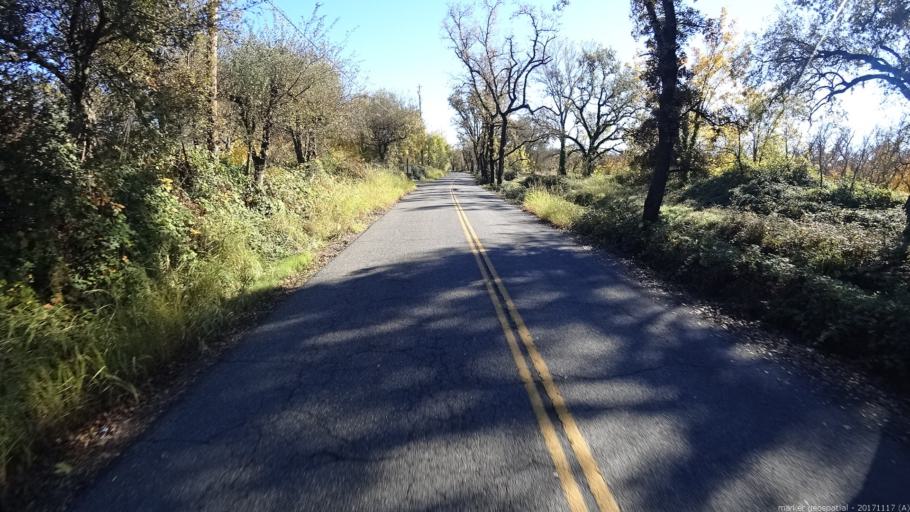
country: US
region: California
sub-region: Shasta County
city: Anderson
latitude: 40.4465
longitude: -122.2487
